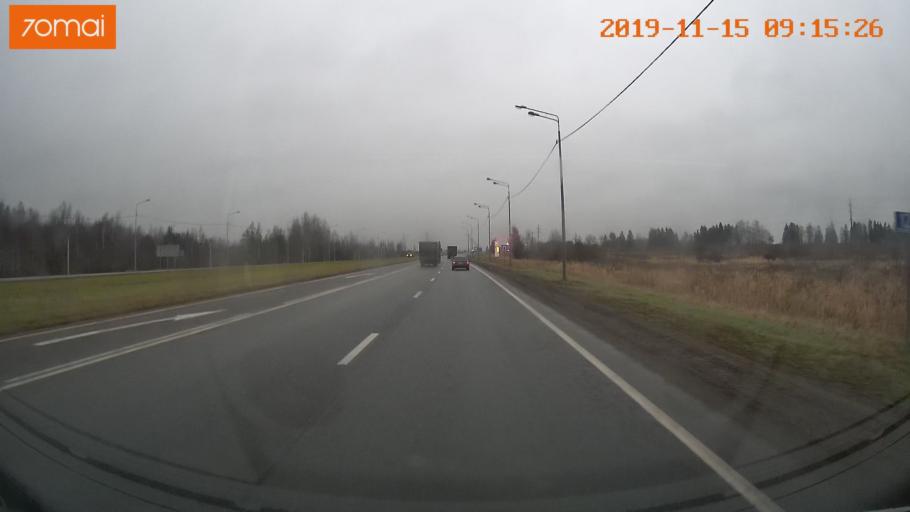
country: RU
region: Vologda
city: Tonshalovo
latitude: 59.2386
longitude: 37.9669
